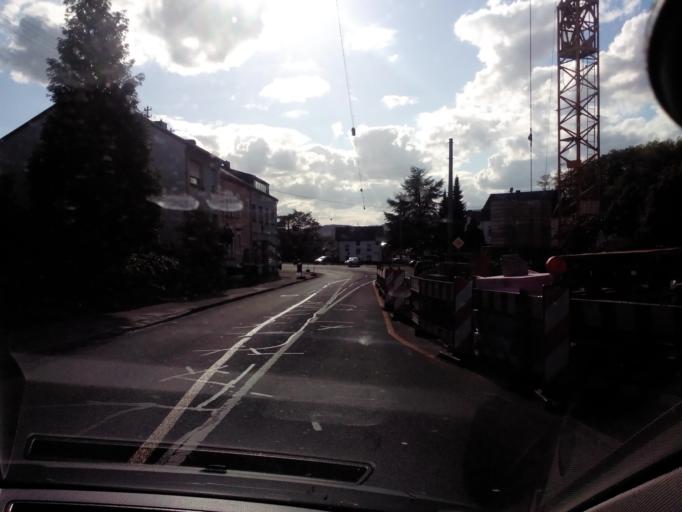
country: DE
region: Saarland
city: Rehlingen-Siersburg
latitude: 49.3650
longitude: 6.6695
